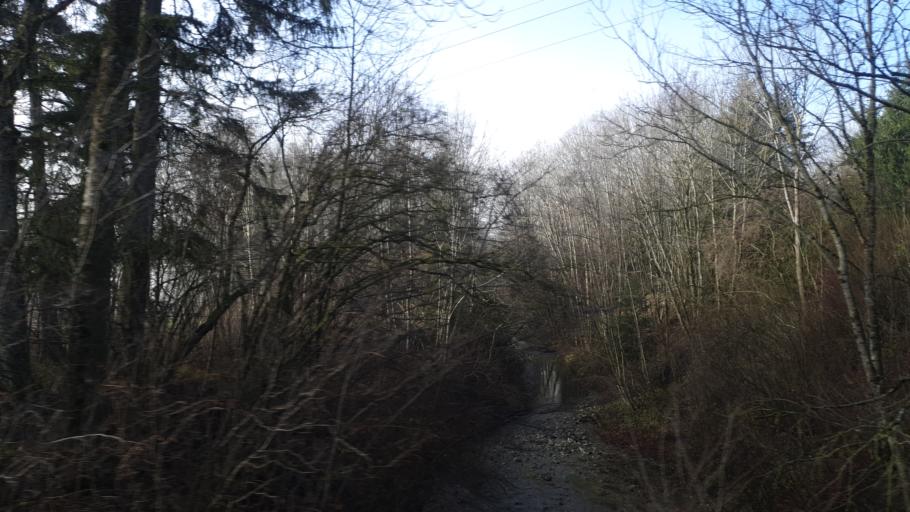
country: CH
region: Fribourg
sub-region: Veveyse District
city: Chatel-Saint-Denis
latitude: 46.5761
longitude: 6.9266
